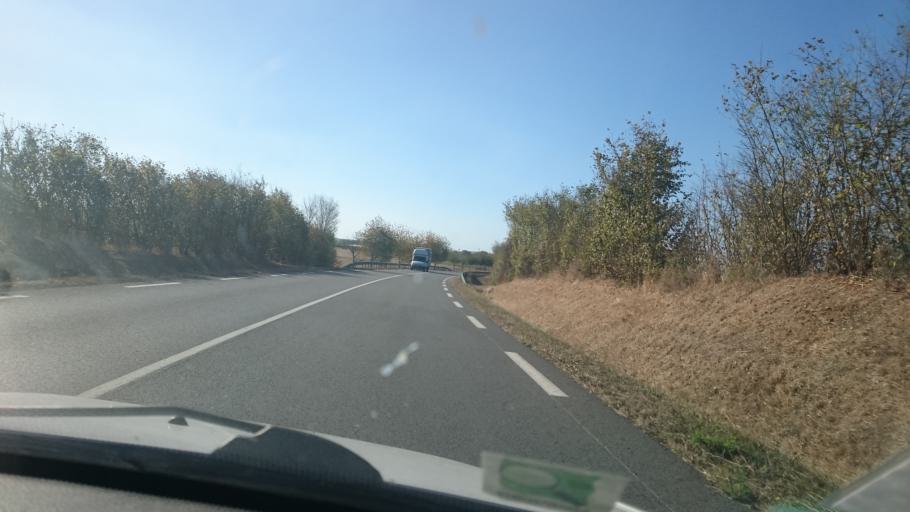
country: FR
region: Centre
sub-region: Departement du Cher
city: Chateaumeillant
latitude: 46.5554
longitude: 2.2057
